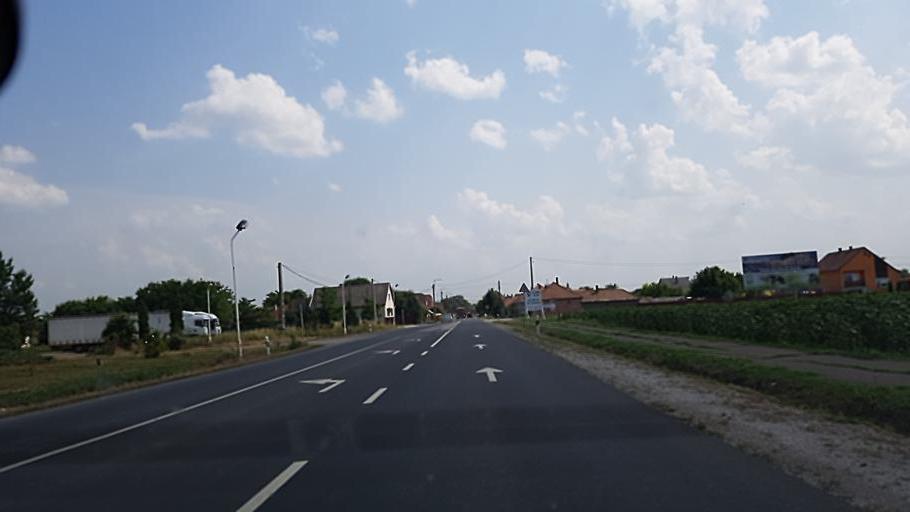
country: HU
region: Heves
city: Besenyotelek
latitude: 47.7103
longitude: 20.4246
